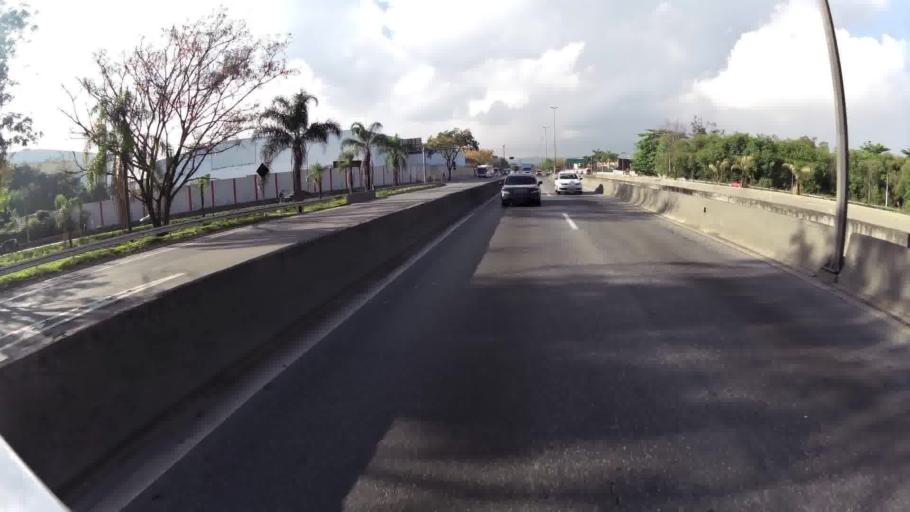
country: BR
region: Rio de Janeiro
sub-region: Duque De Caxias
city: Duque de Caxias
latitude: -22.8092
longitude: -43.2887
